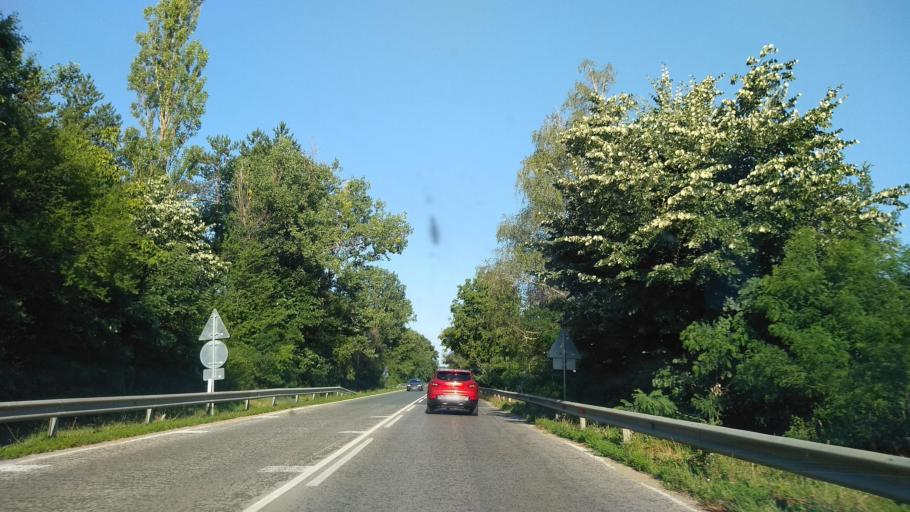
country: BG
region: Lovech
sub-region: Obshtina Teteven
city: Teteven
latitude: 43.0547
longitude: 24.2573
